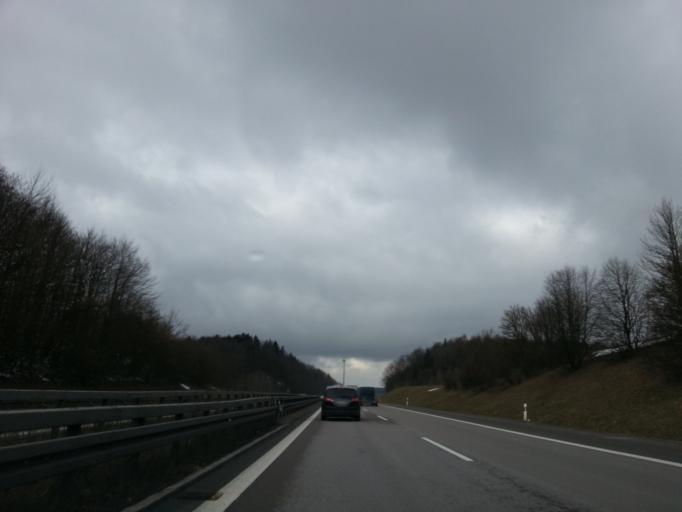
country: DE
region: Bavaria
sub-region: Upper Palatinate
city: Brunn
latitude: 49.1330
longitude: 11.8669
